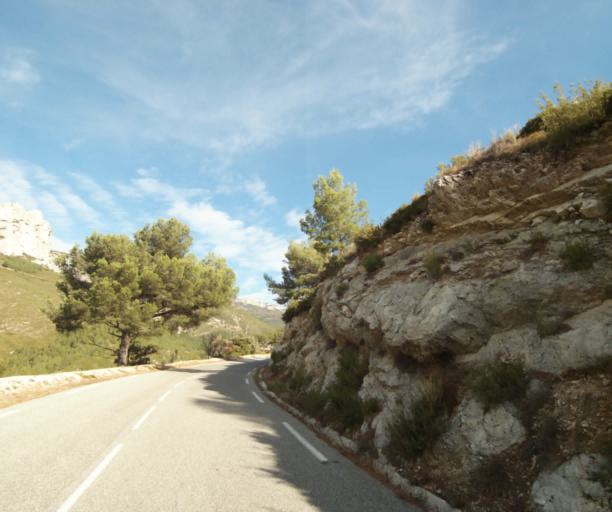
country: FR
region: Provence-Alpes-Cote d'Azur
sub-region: Departement des Bouches-du-Rhone
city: Gemenos
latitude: 43.2937
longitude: 5.6580
